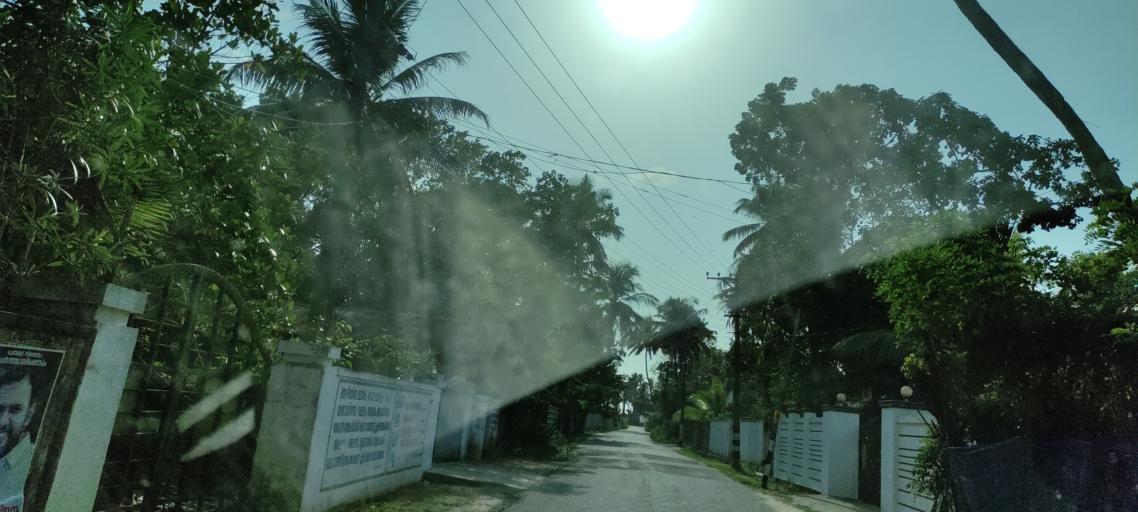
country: IN
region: Kerala
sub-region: Alappuzha
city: Vayalar
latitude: 9.6859
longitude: 76.2928
